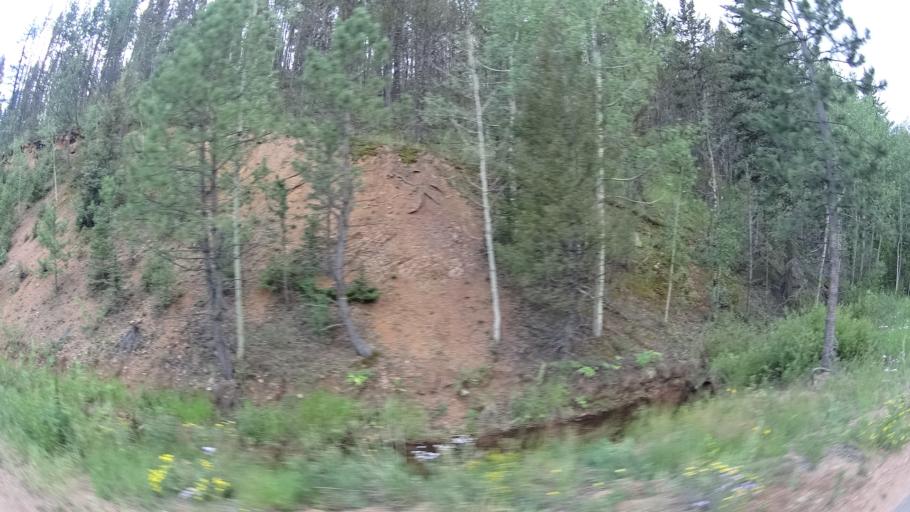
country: US
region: Colorado
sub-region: El Paso County
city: Cascade-Chipita Park
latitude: 38.9005
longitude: -104.9920
